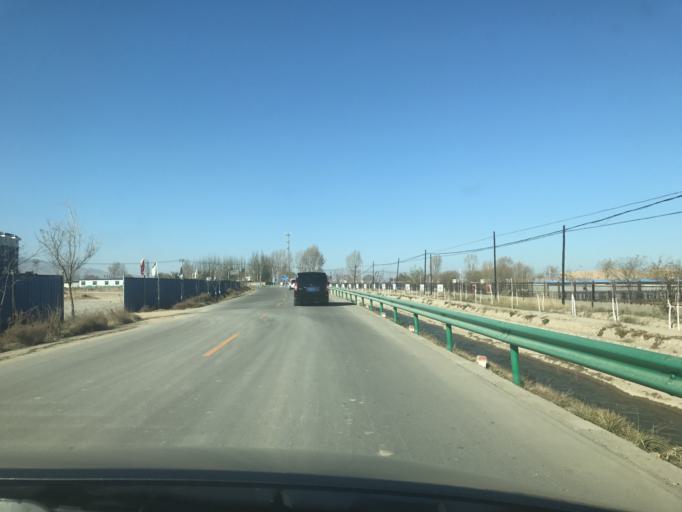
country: CN
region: Gansu Sheng
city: Gulang
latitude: 37.6767
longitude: 102.8383
